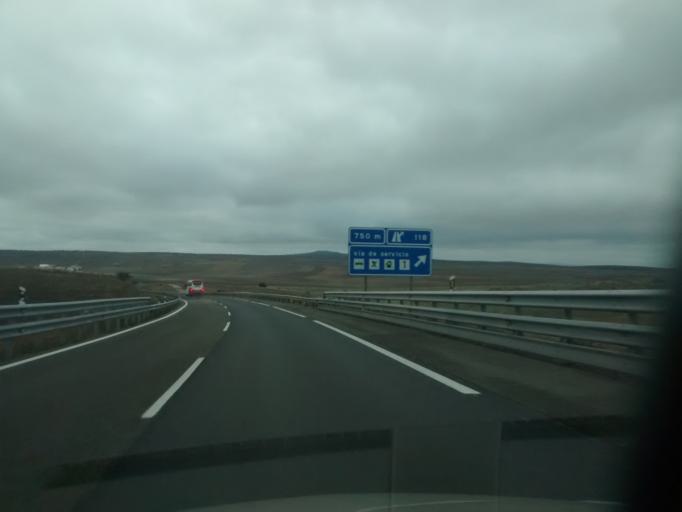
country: ES
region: Castille-La Mancha
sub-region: Provincia de Guadalajara
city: Torremocha del Campo
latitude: 40.9906
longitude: -2.5979
